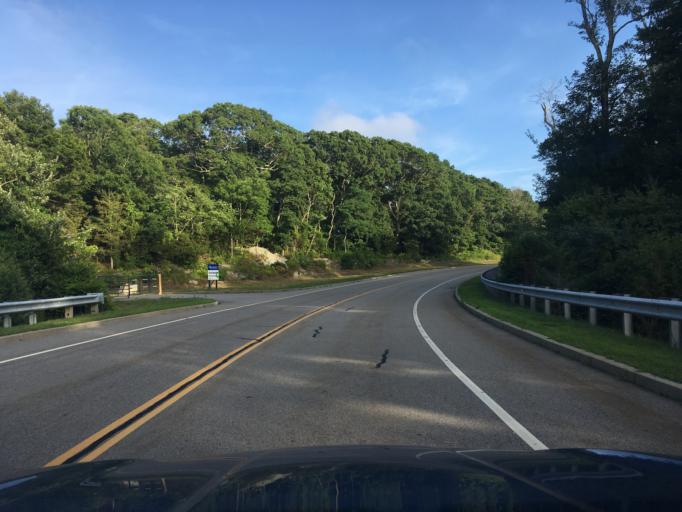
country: US
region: Rhode Island
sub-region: Kent County
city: East Greenwich
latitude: 41.6043
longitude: -71.4260
